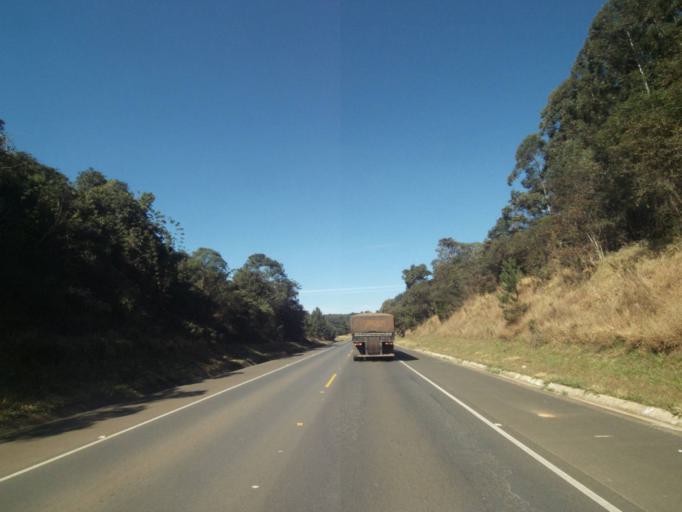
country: BR
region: Parana
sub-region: Tibagi
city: Tibagi
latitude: -24.5737
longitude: -50.4511
